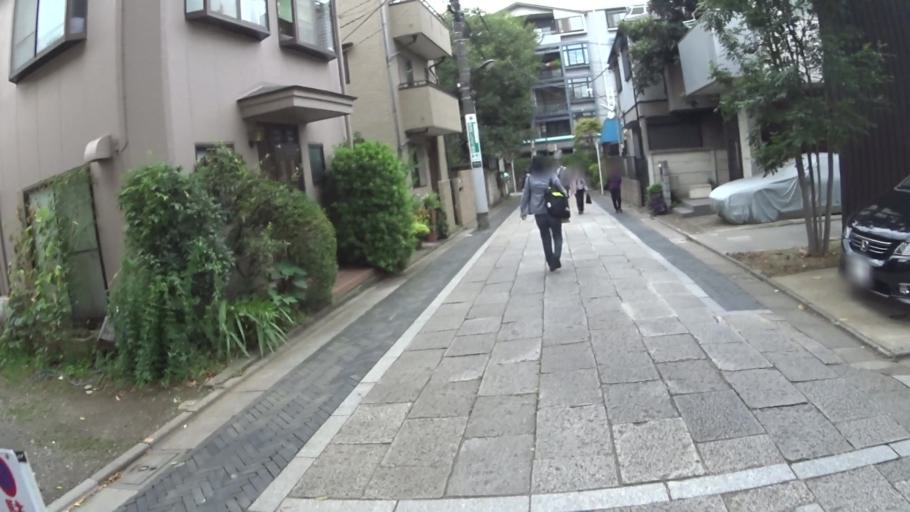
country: JP
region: Tokyo
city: Tokyo
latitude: 35.7217
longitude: 139.7145
